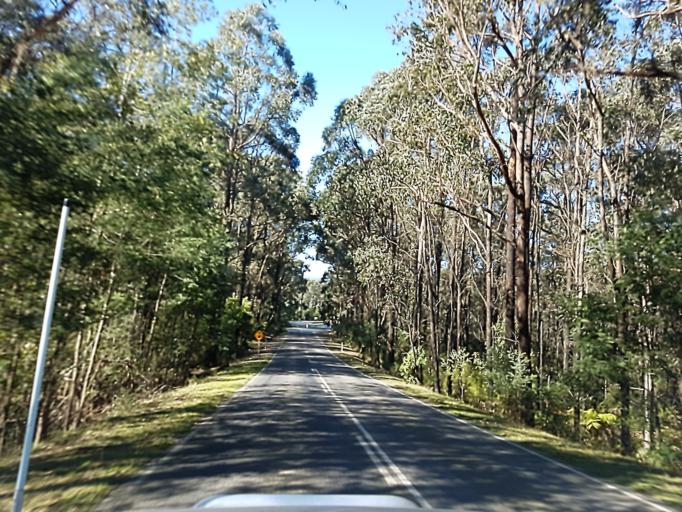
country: AU
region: Victoria
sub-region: Yarra Ranges
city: Yarra Glen
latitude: -37.5262
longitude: 145.4158
